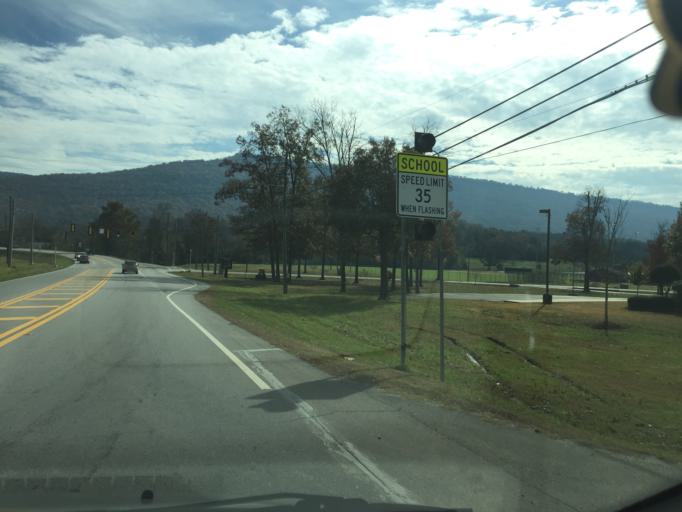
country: US
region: Georgia
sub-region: Dade County
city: Trenton
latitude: 34.8642
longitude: -85.5068
